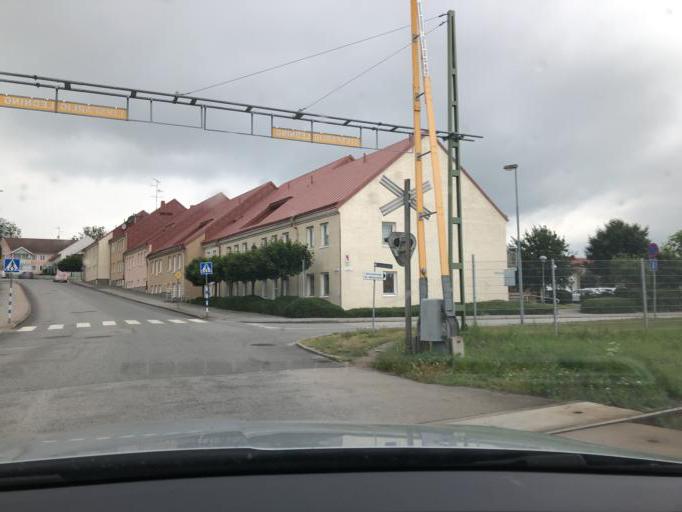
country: SE
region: Blekinge
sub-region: Solvesborgs Kommun
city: Soelvesborg
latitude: 56.0524
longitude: 14.5896
